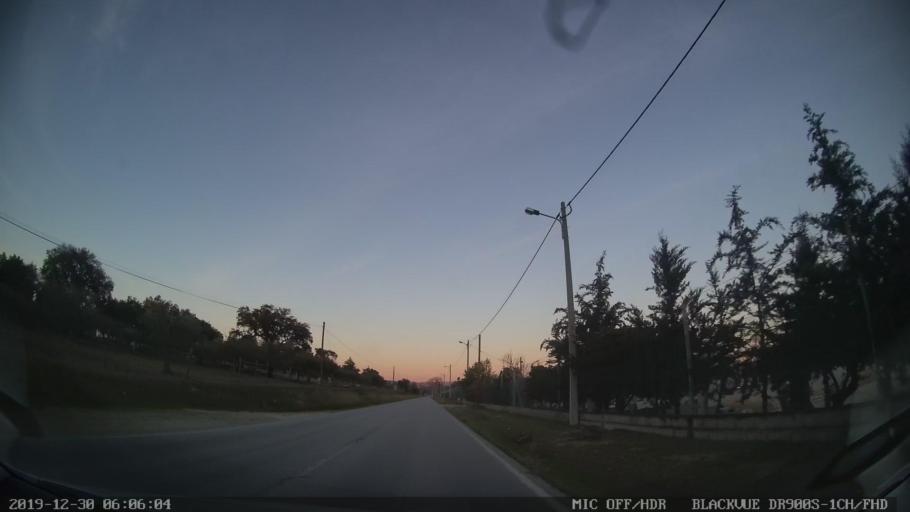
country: PT
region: Castelo Branco
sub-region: Penamacor
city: Penamacor
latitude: 40.0957
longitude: -7.2336
